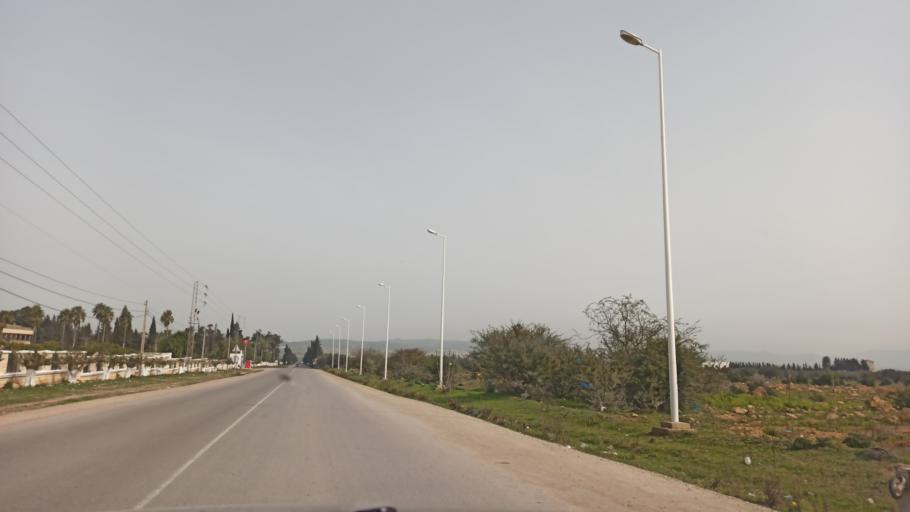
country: TN
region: Zaghwan
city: Zaghouan
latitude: 36.4248
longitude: 10.0942
